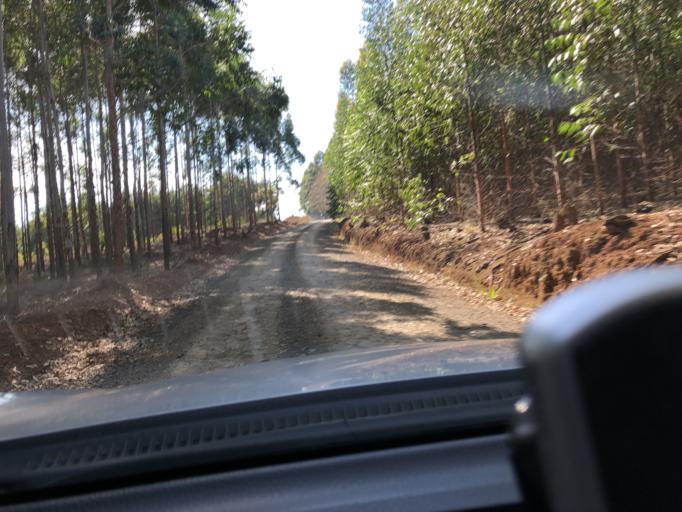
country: ZA
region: KwaZulu-Natal
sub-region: Sisonke District Municipality
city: Ixopo
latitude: -30.1827
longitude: 30.0548
